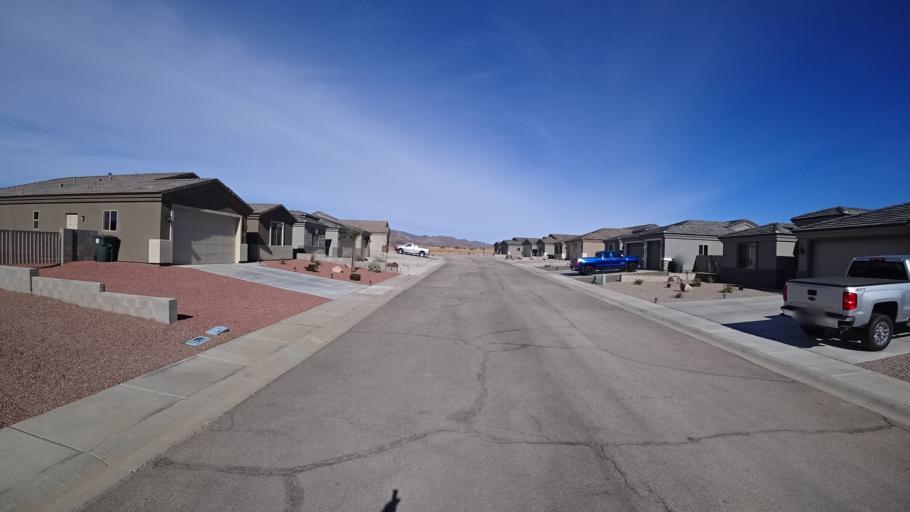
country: US
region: Arizona
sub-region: Mohave County
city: New Kingman-Butler
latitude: 35.2773
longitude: -114.0360
